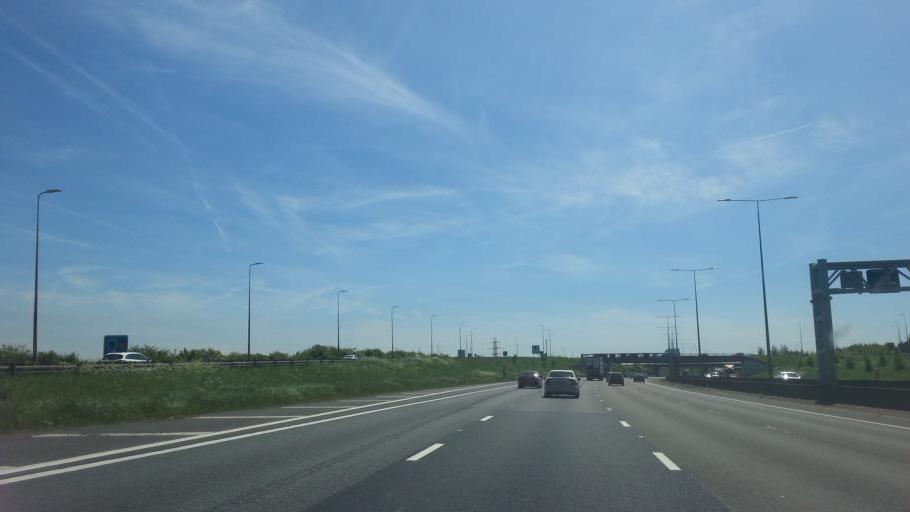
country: GB
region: England
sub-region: Luton
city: Luton
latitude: 51.8570
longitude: -0.4261
